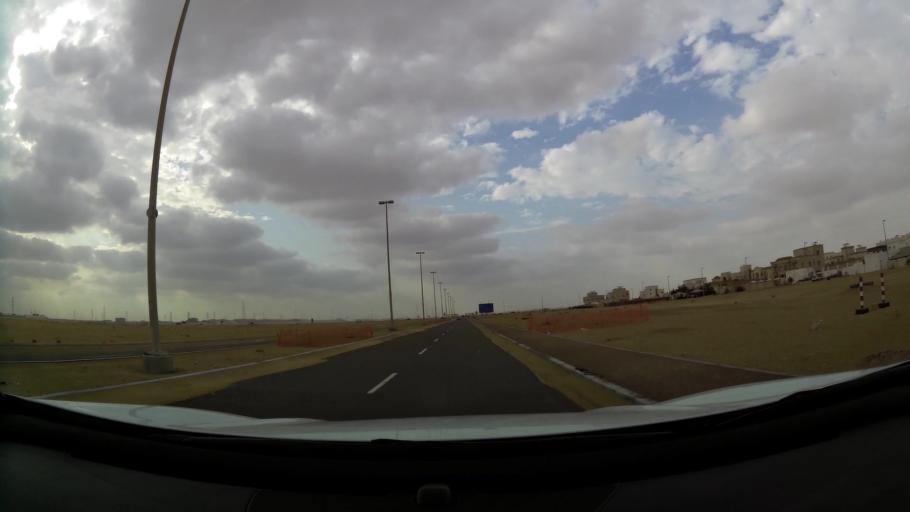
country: AE
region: Abu Dhabi
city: Abu Dhabi
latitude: 24.3462
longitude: 54.6096
